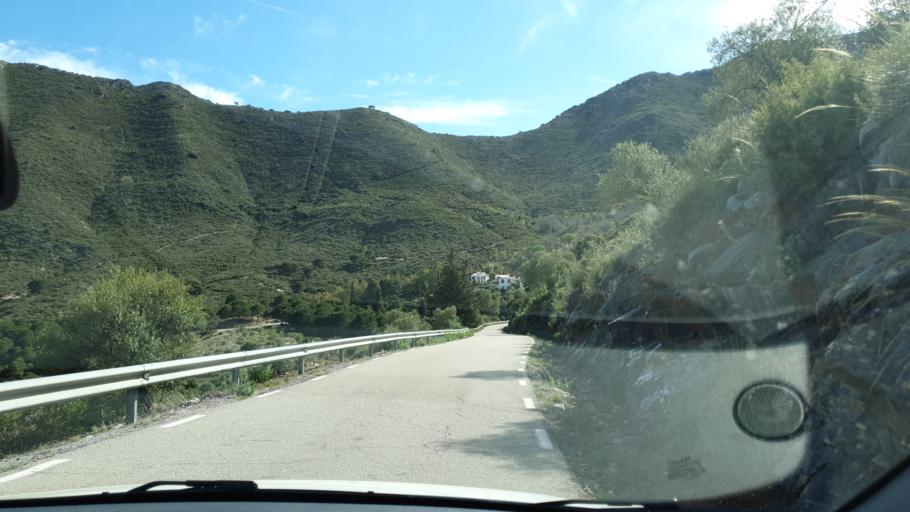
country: ES
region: Andalusia
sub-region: Provincia de Malaga
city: Ojen
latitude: 36.5904
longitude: -4.8716
